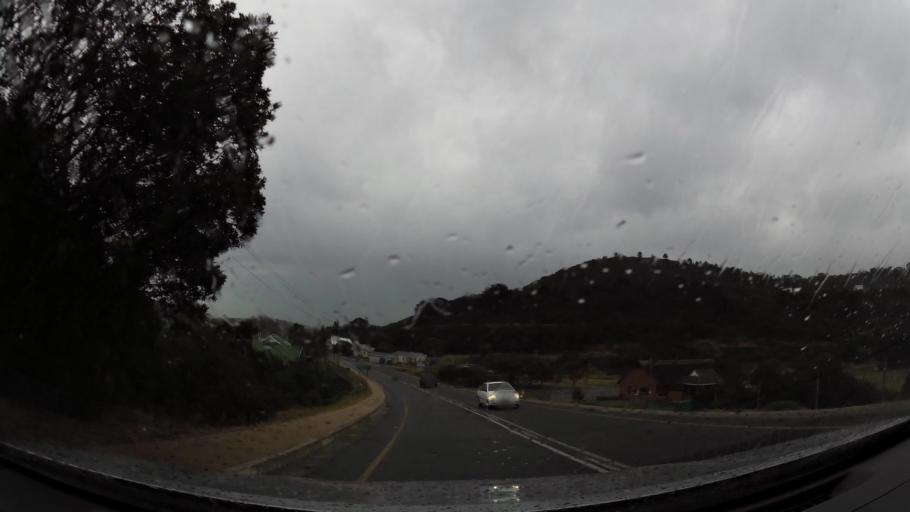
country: ZA
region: Western Cape
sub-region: Eden District Municipality
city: Mossel Bay
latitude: -34.0493
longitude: 22.2399
